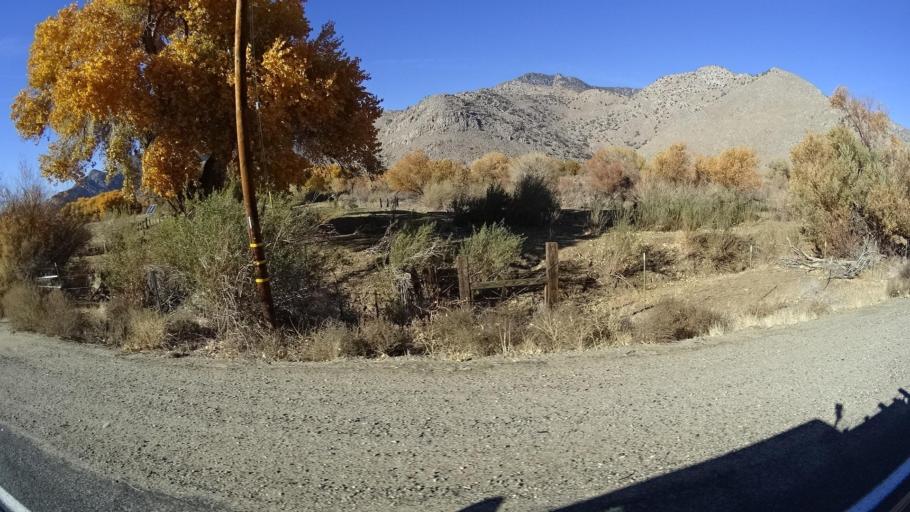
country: US
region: California
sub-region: Kern County
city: Weldon
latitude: 35.6846
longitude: -118.2445
